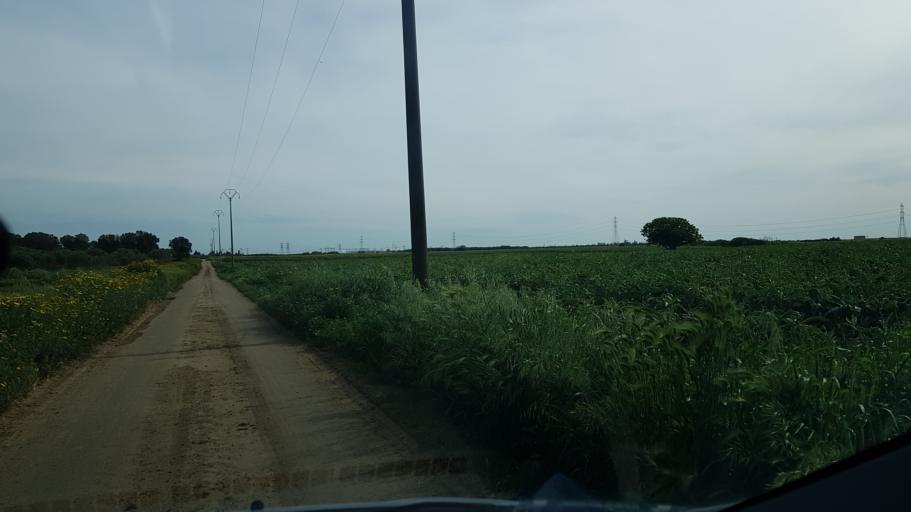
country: IT
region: Apulia
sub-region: Provincia di Brindisi
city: Tuturano
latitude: 40.5758
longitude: 17.9208
